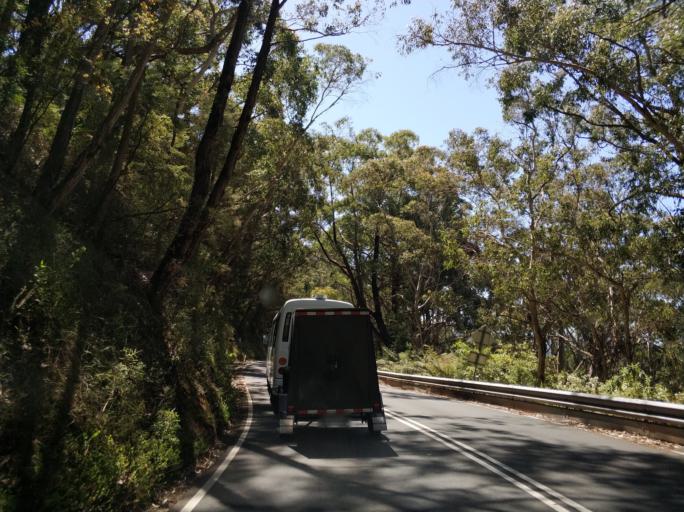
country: AU
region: Victoria
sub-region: Colac-Otway
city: Apollo Bay
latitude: -38.7446
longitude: 143.2569
